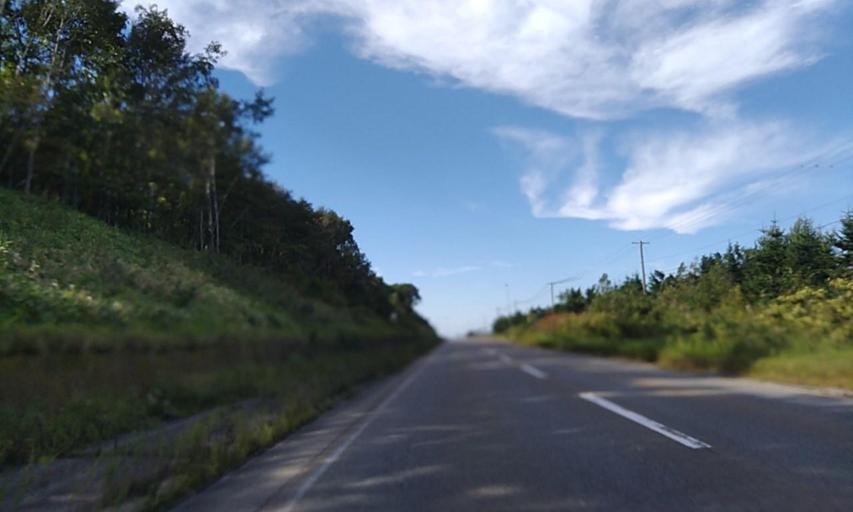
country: JP
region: Hokkaido
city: Obihiro
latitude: 42.8329
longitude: 143.4666
